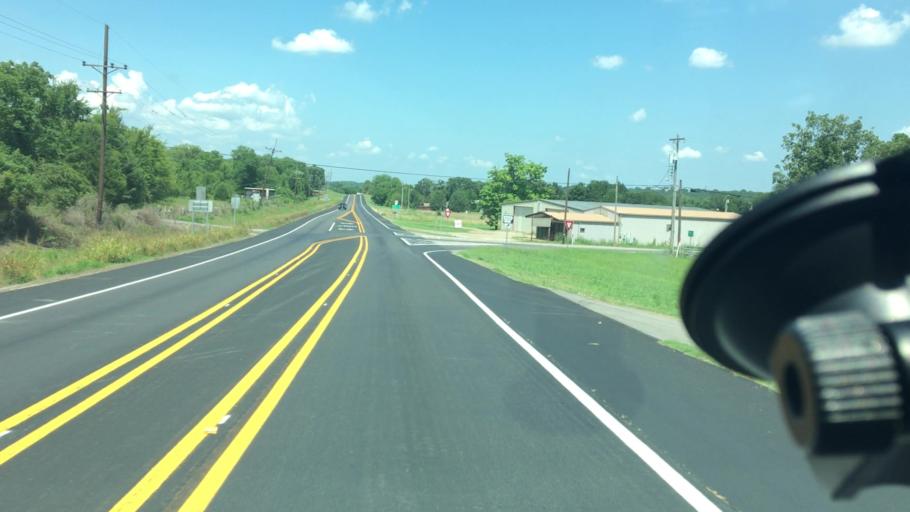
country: US
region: Arkansas
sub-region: Sebastian County
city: Lavaca
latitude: 35.3018
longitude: -94.1618
